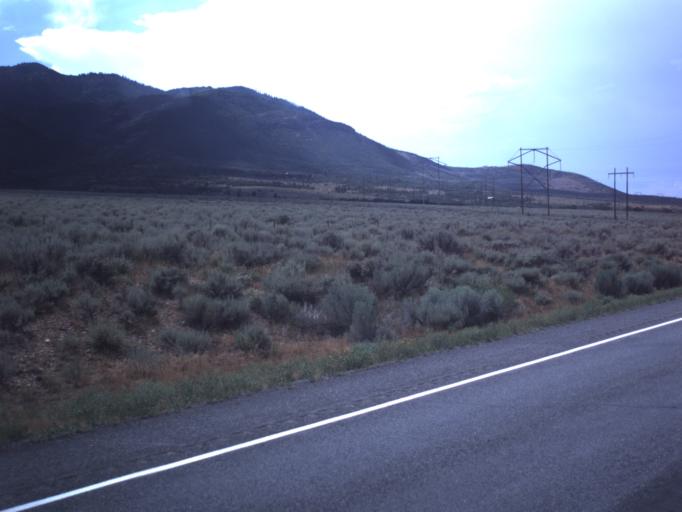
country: US
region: Utah
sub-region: Sanpete County
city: Fountain Green
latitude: 39.6912
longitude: -111.6862
